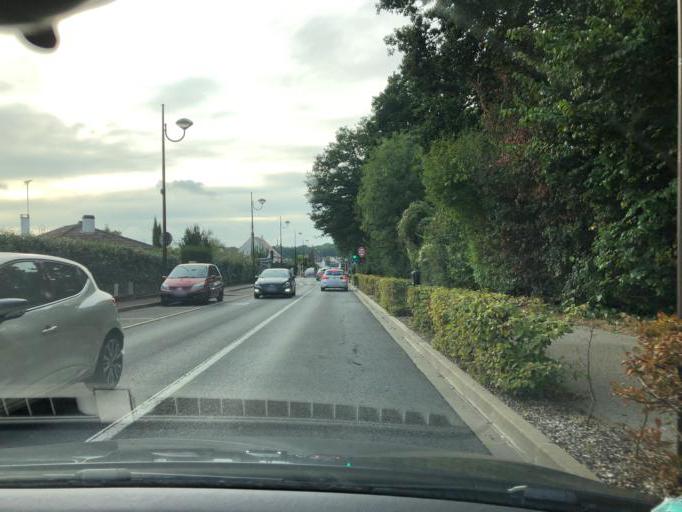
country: FR
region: Ile-de-France
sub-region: Departement des Yvelines
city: Velizy-Villacoublay
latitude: 48.7874
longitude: 2.1839
